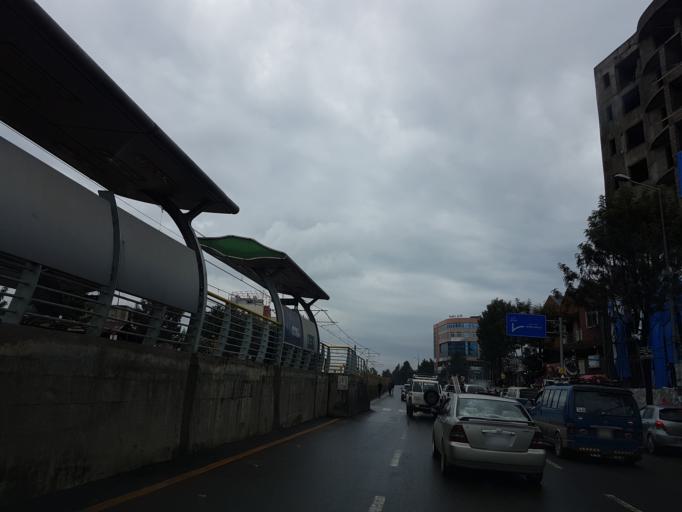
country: ET
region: Adis Abeba
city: Addis Ababa
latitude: 9.0189
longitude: 38.8199
